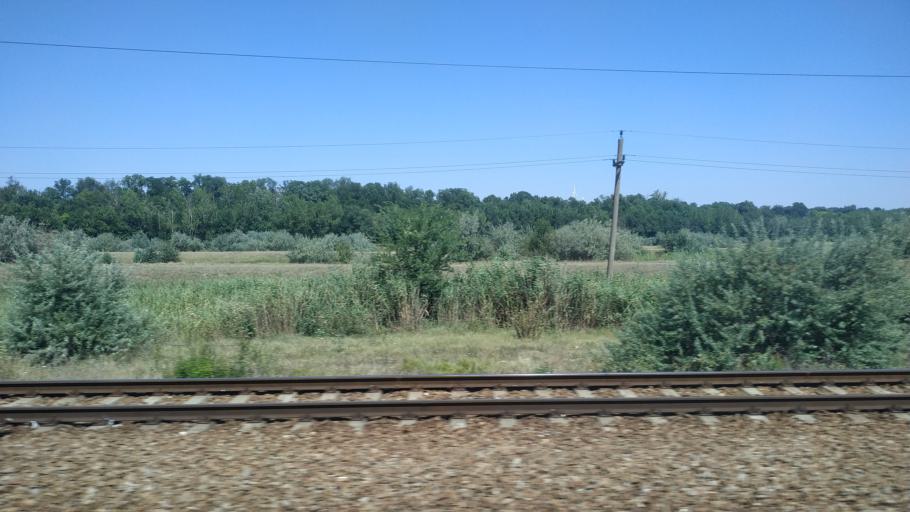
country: RO
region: Constanta
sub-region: Comuna Mircea Voda
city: Mircea Voda
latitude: 44.2654
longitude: 28.1494
